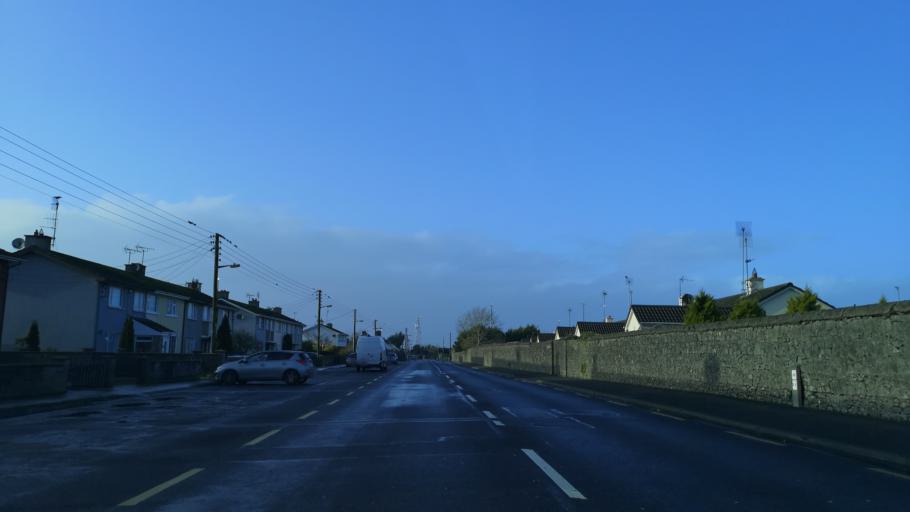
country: IE
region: Connaught
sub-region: County Galway
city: Tuam
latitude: 53.5087
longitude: -8.8408
